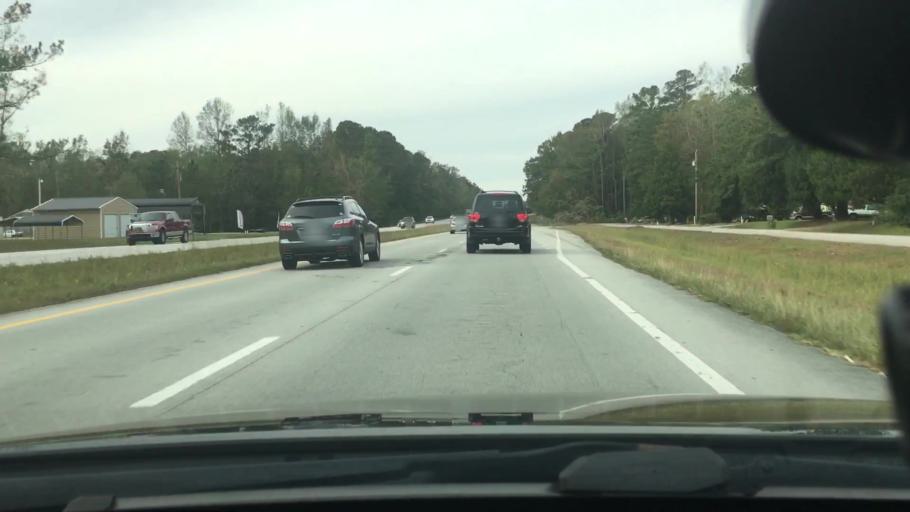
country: US
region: North Carolina
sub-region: Craven County
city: Fairfield Harbour
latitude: 35.0236
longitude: -76.9993
